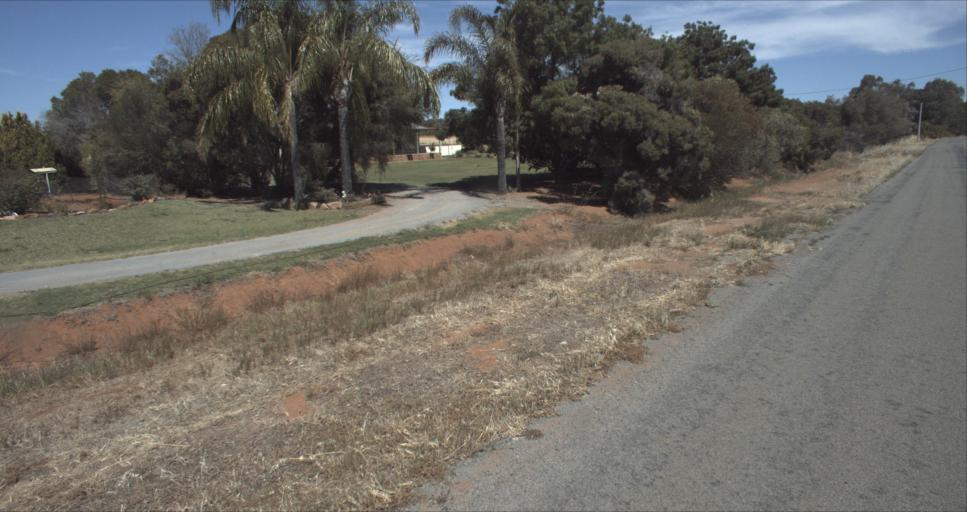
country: AU
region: New South Wales
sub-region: Leeton
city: Leeton
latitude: -34.5974
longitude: 146.4373
